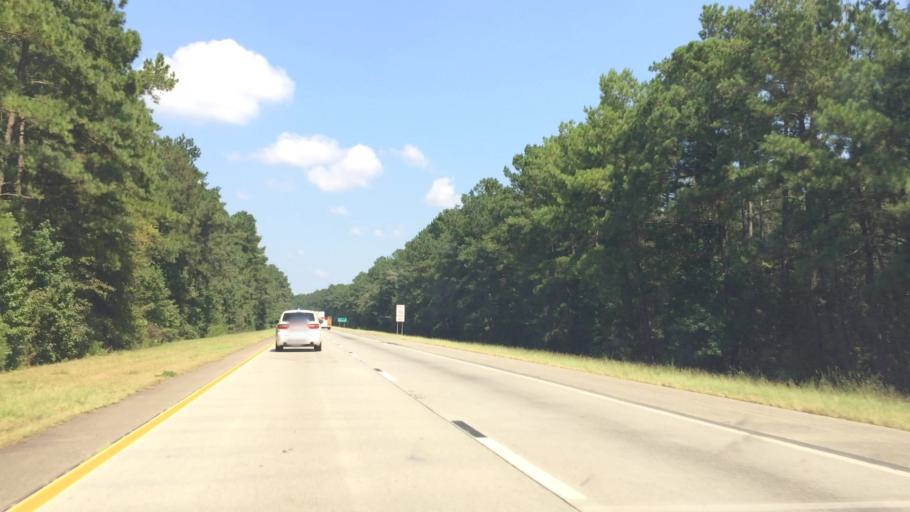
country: US
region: South Carolina
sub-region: Colleton County
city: Walterboro
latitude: 33.0136
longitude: -80.6666
